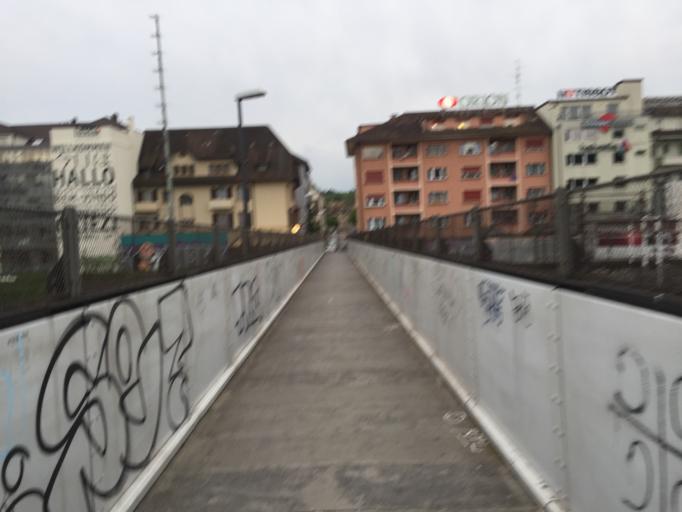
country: CH
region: Basel-City
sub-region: Basel-Stadt
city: Basel
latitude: 47.5453
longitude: 7.5956
